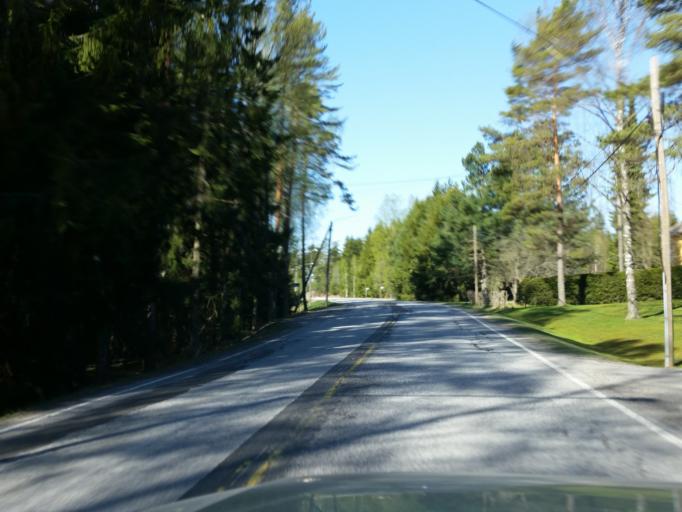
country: FI
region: Uusimaa
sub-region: Helsinki
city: Lohja
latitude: 60.1740
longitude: 24.1105
